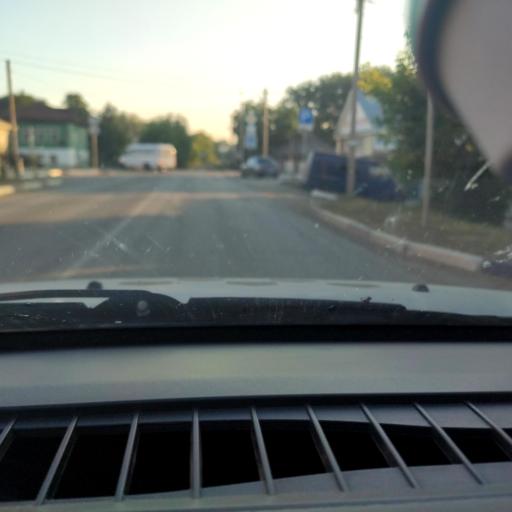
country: RU
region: Perm
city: Kungur
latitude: 57.4408
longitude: 56.9516
